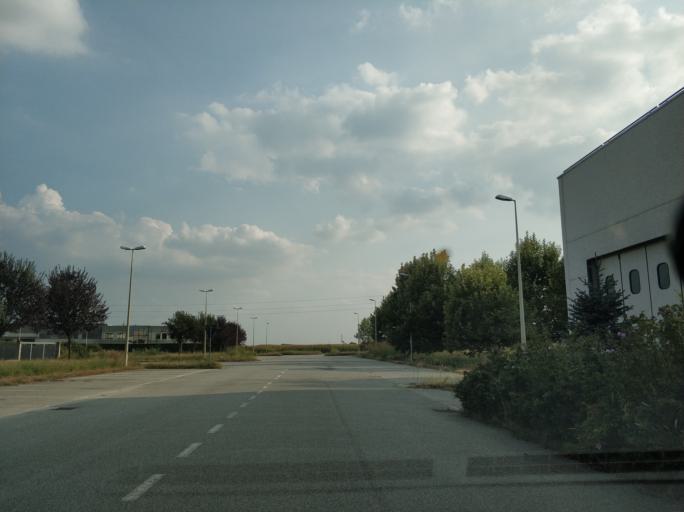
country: IT
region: Piedmont
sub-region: Provincia di Torino
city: Cirie
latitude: 45.2116
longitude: 7.6093
